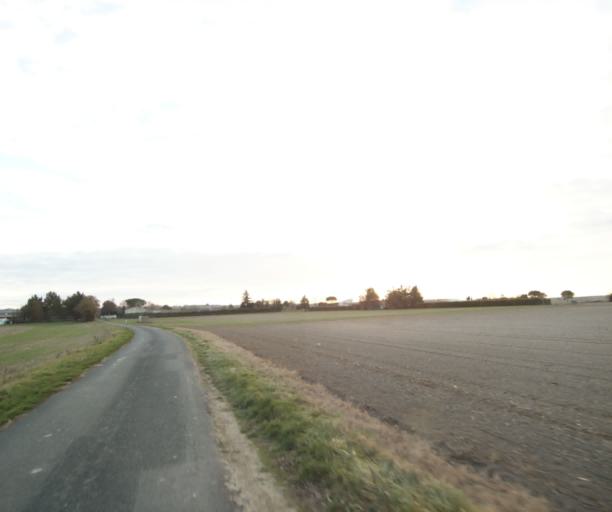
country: FR
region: Poitou-Charentes
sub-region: Departement de la Charente-Maritime
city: Les Gonds
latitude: 45.7003
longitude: -0.6177
